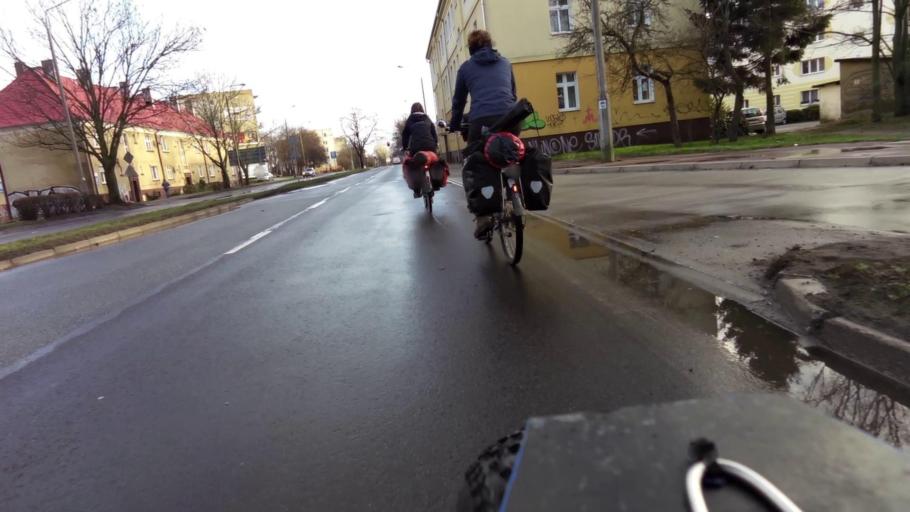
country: PL
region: Lubusz
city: Gorzow Wielkopolski
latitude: 52.7348
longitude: 15.2093
